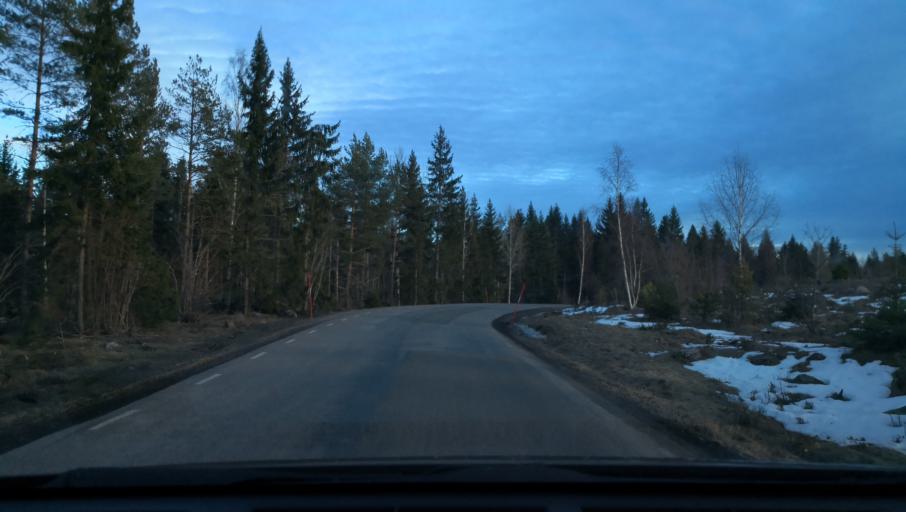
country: SE
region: Uppsala
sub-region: Osthammars Kommun
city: Osterbybruk
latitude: 60.2306
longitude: 17.9183
